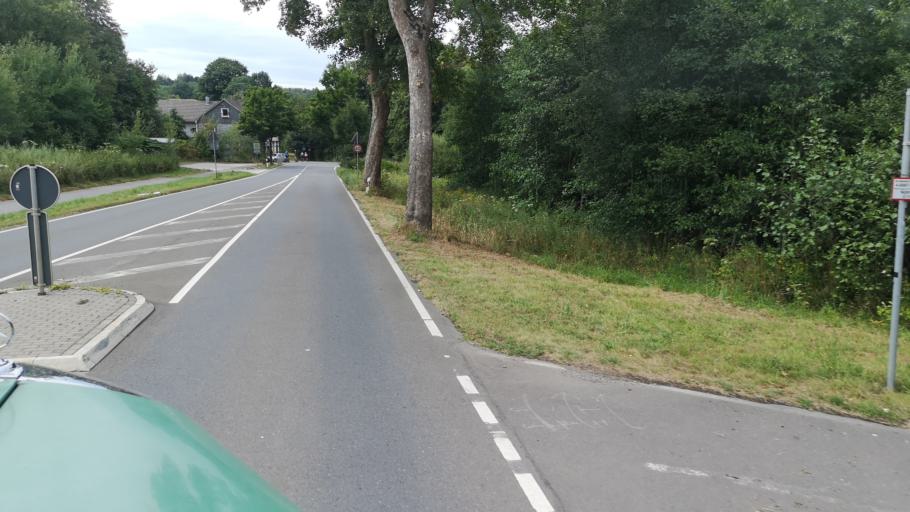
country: DE
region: North Rhine-Westphalia
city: Huckeswagen
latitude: 51.1468
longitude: 7.2968
